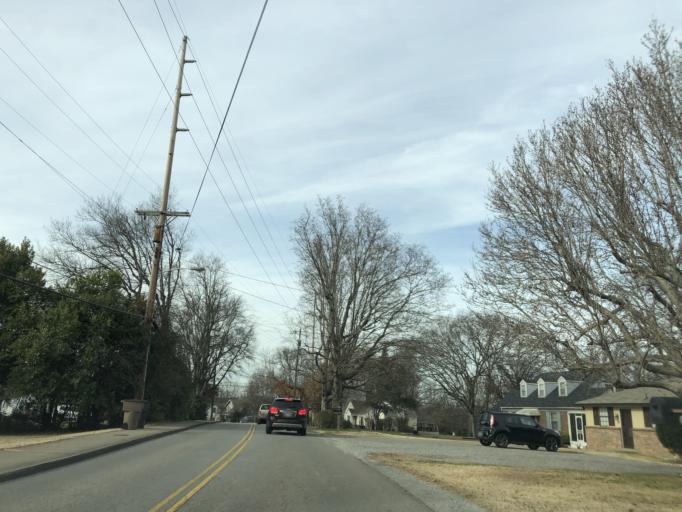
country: US
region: Tennessee
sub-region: Davidson County
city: Nashville
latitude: 36.2126
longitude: -86.7209
